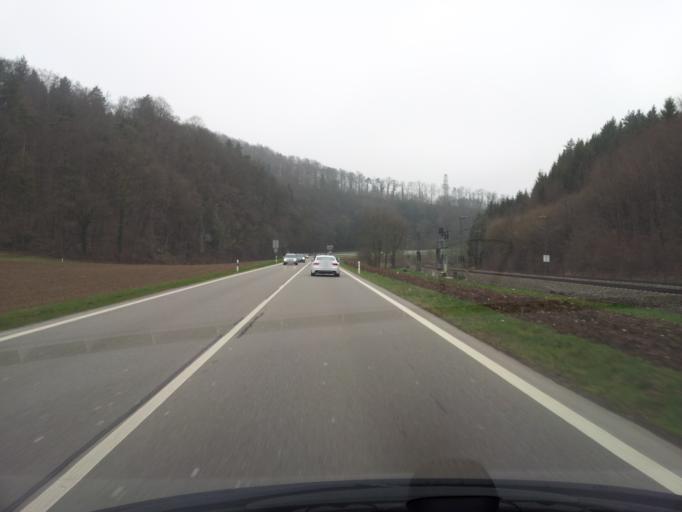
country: CH
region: Schaffhausen
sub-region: Bezirk Reiat
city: Thayngen
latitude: 47.7399
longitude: 8.6910
